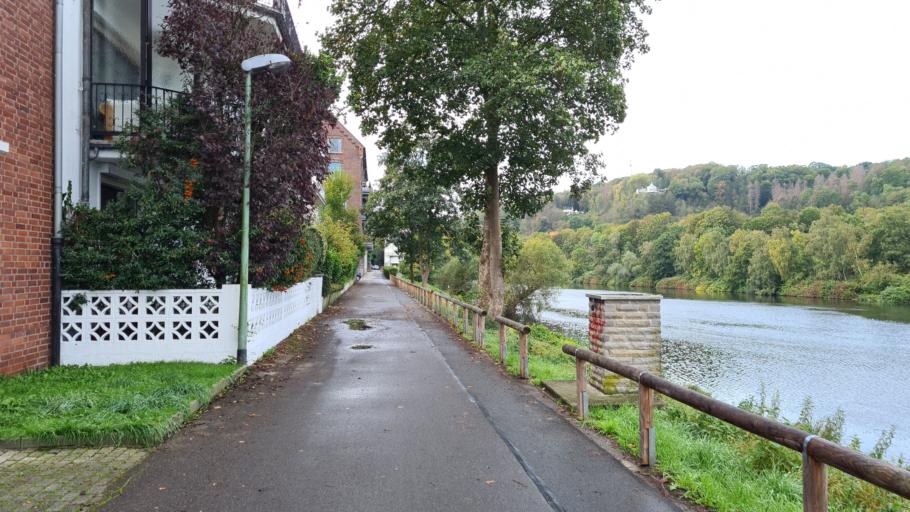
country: DE
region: North Rhine-Westphalia
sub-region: Regierungsbezirk Dusseldorf
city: Essen
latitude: 51.3957
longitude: 7.0021
